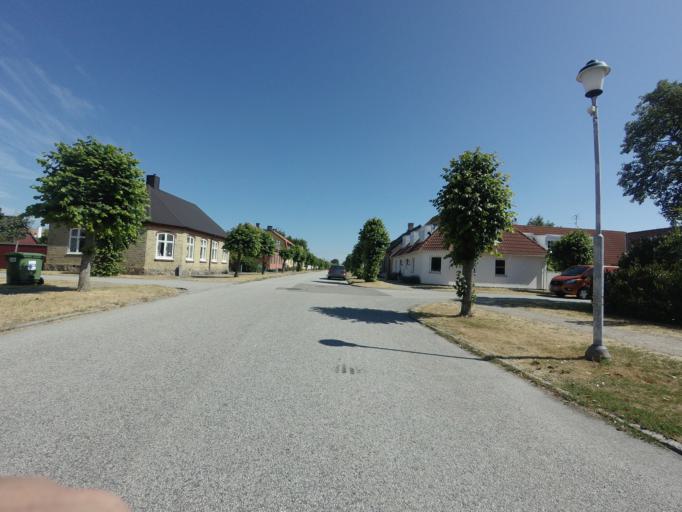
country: SE
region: Skane
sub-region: Vellinge Kommun
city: Skanor med Falsterbo
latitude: 55.4154
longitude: 12.8453
